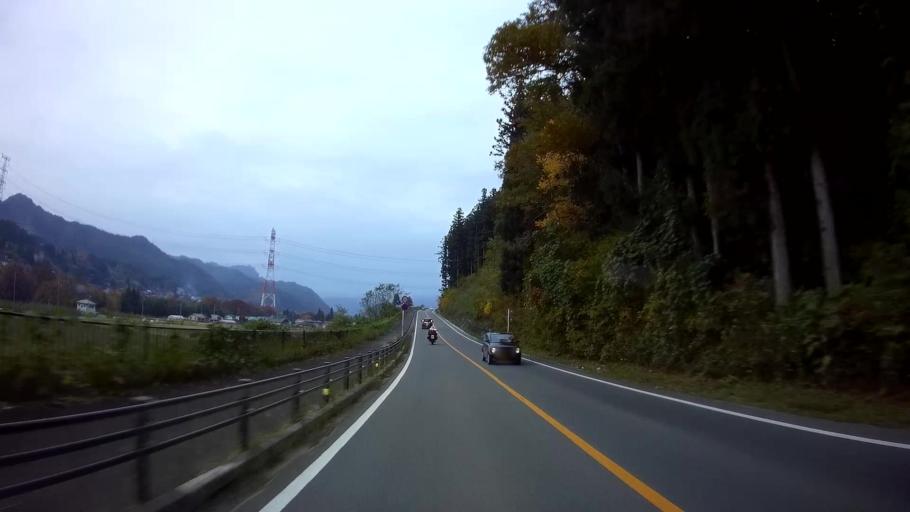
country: JP
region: Gunma
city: Nakanojomachi
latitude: 36.5639
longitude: 138.7480
